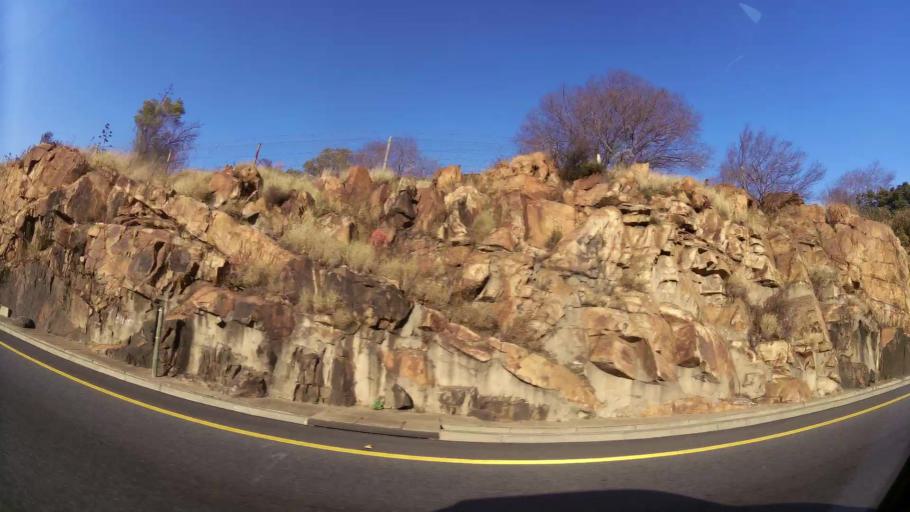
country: ZA
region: Gauteng
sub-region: Ekurhuleni Metropolitan Municipality
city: Germiston
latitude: -26.2543
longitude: 28.1219
